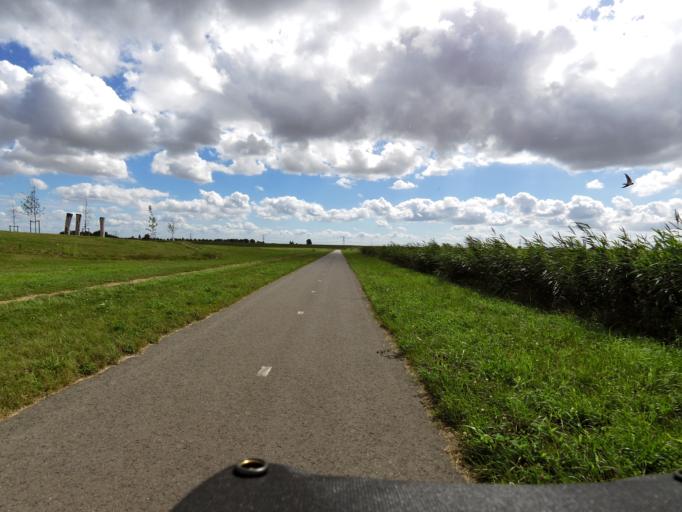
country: NL
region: South Holland
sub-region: Gemeente Oud-Beijerland
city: Oud-Beijerland
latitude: 51.8237
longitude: 4.3691
